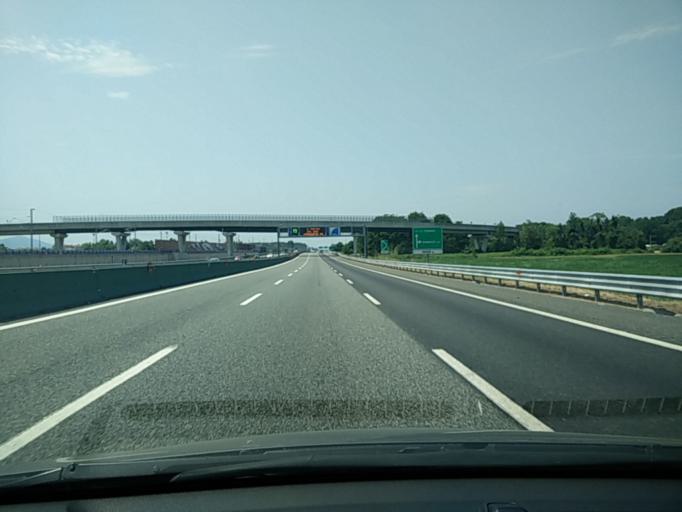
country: IT
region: Piedmont
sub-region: Provincia di Torino
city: Brandizzo
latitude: 45.1882
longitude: 7.8413
